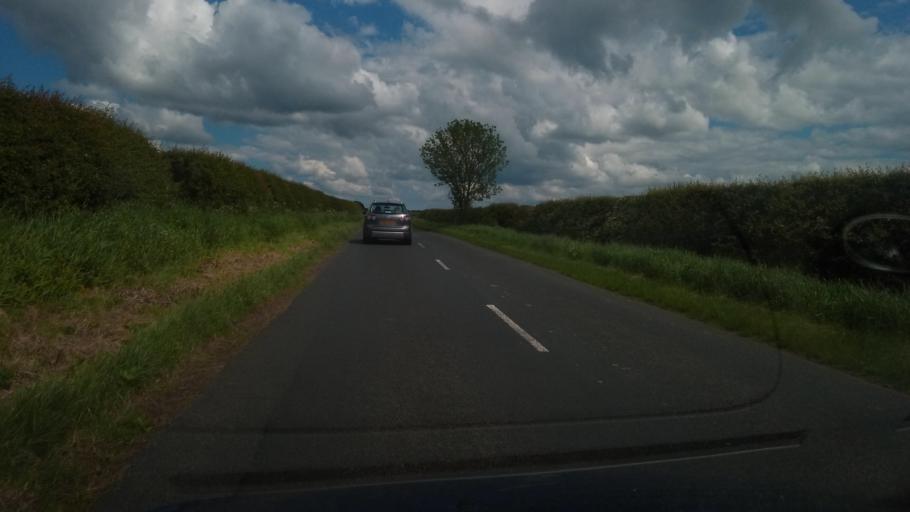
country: GB
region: Scotland
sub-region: The Scottish Borders
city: Kelso
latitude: 55.5885
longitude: -2.3720
